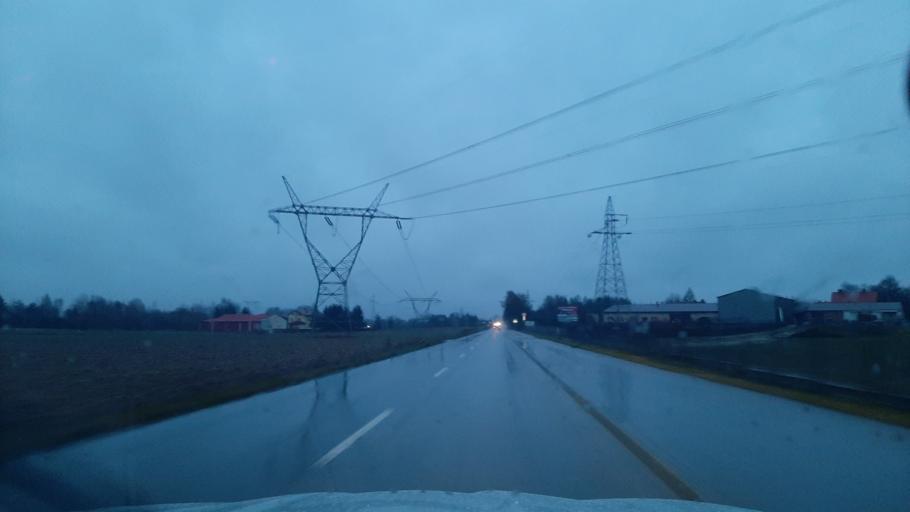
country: PL
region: Lublin Voivodeship
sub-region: Powiat lubelski
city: Jastkow
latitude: 51.3360
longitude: 22.5028
